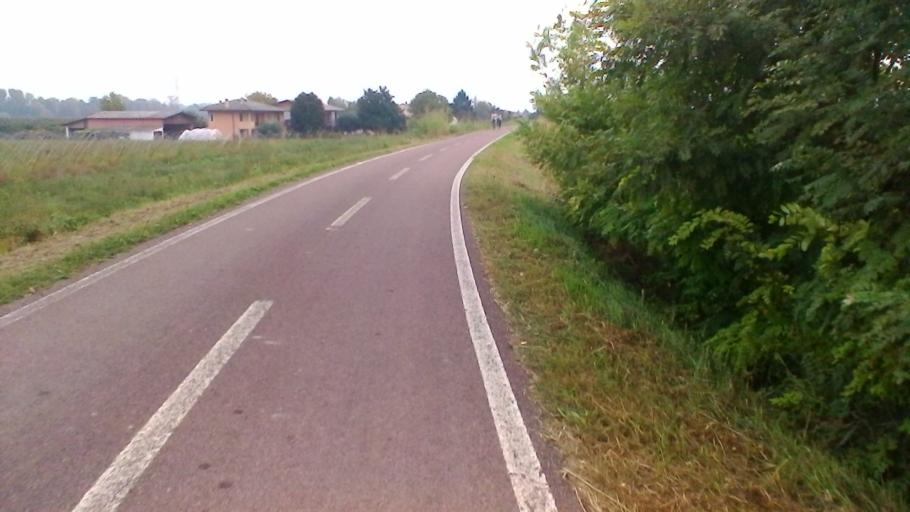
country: IT
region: Veneto
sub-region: Provincia di Verona
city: San Martino Buon Albergo
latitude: 45.3904
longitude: 11.0750
